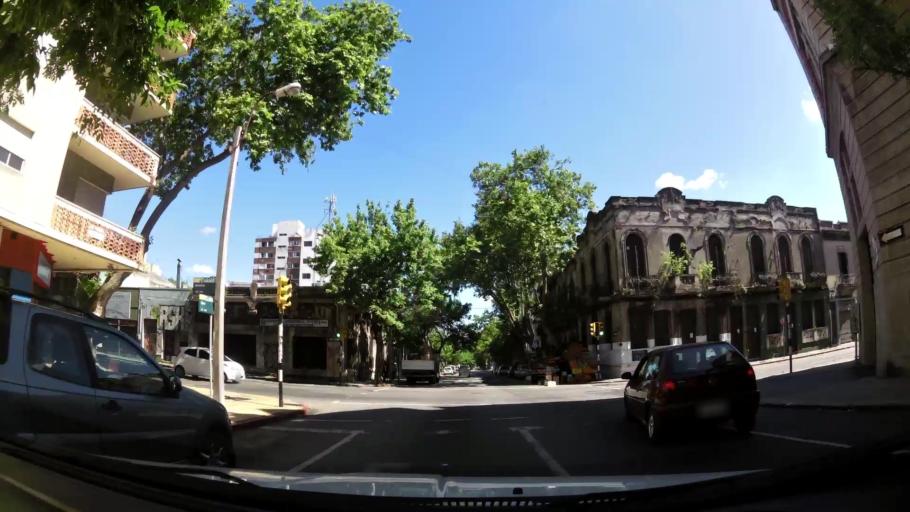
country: UY
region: Montevideo
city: Montevideo
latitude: -34.9022
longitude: -56.1815
